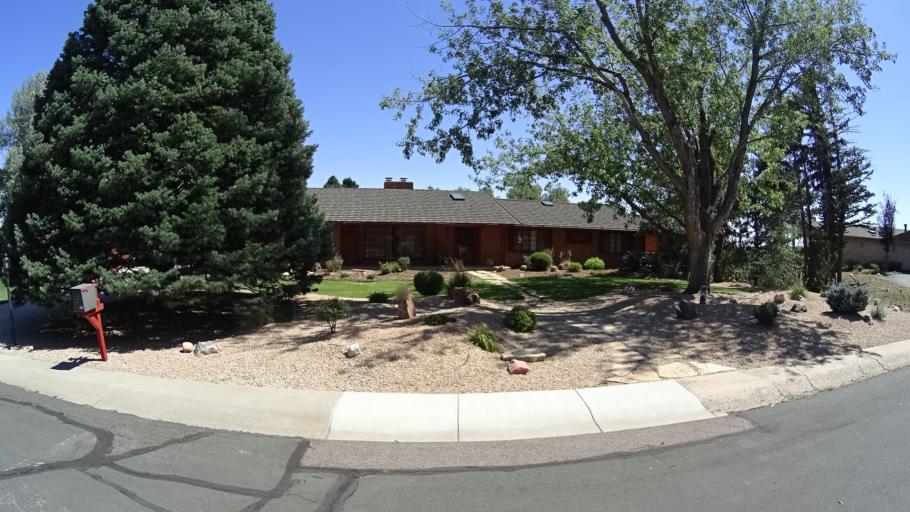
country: US
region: Colorado
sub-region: El Paso County
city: Colorado Springs
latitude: 38.7855
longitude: -104.8300
